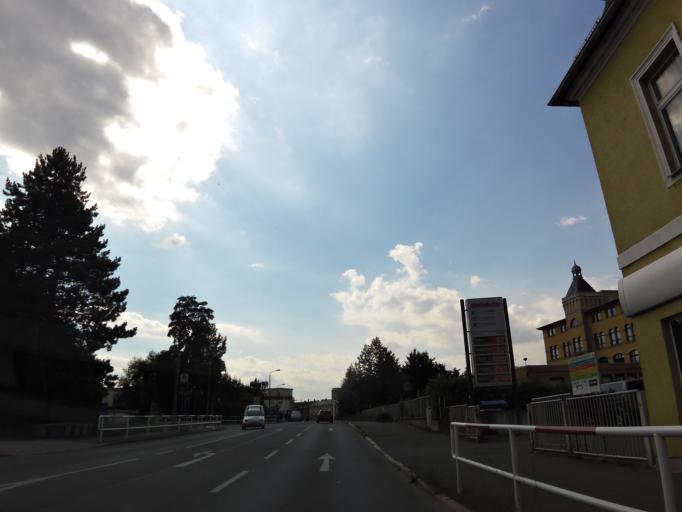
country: DE
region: Saxony
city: Glauchau
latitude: 50.8248
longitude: 12.5416
